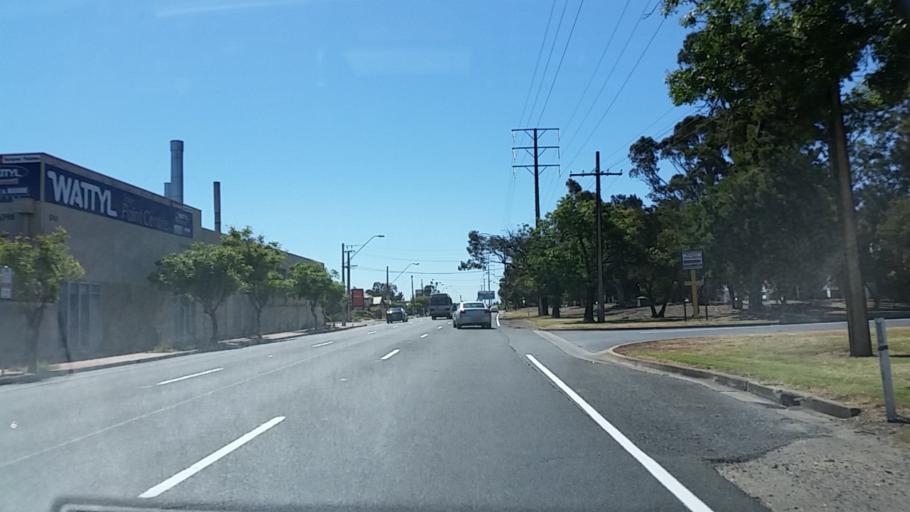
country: AU
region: South Australia
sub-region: Charles Sturt
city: Albert Park
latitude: -34.8713
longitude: 138.5206
